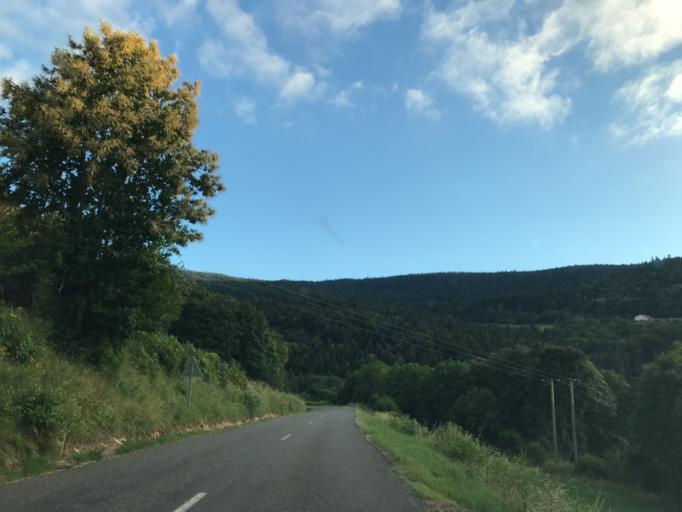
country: FR
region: Rhone-Alpes
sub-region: Departement de la Loire
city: Noiretable
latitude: 45.7790
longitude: 3.7877
